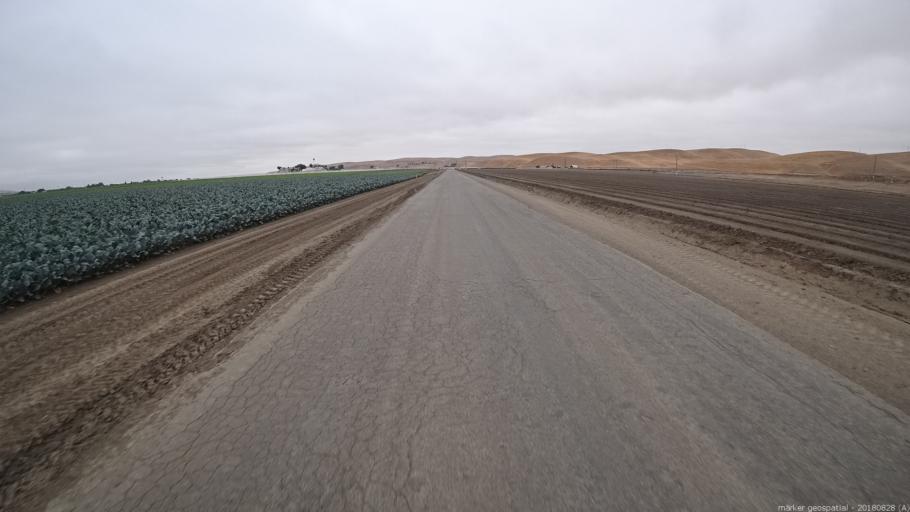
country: US
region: California
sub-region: San Luis Obispo County
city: Lake Nacimiento
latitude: 36.0041
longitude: -120.8861
